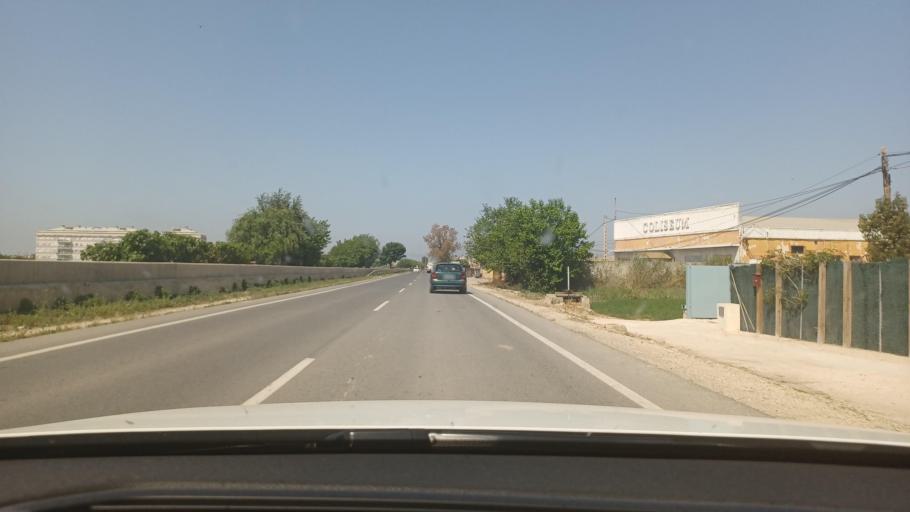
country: ES
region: Valencia
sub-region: Provincia de Alicante
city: Dolores
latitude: 38.1394
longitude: -0.7558
